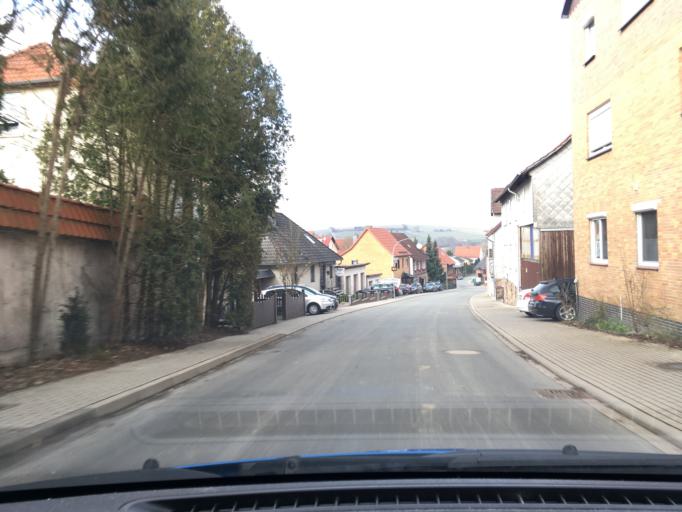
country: DE
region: Lower Saxony
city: Uslar
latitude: 51.6213
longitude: 9.6215
